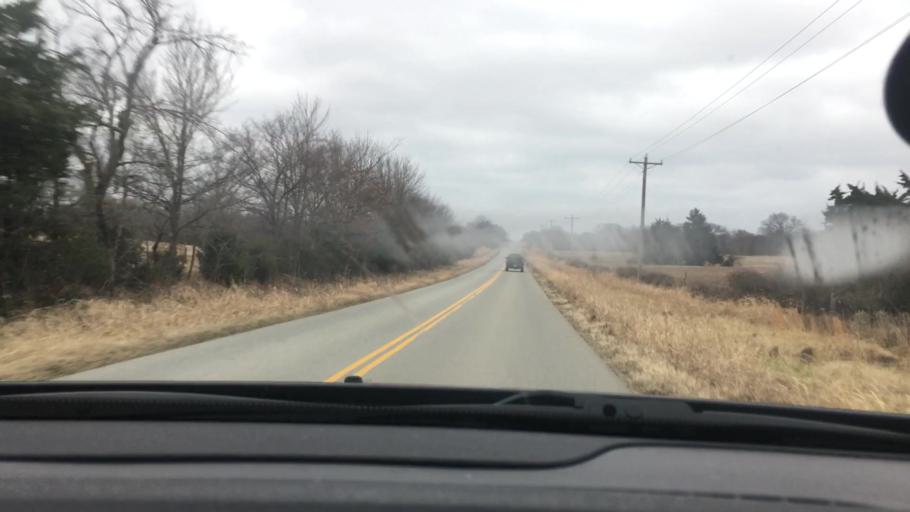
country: US
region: Oklahoma
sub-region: Atoka County
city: Atoka
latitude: 34.3208
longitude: -96.0755
